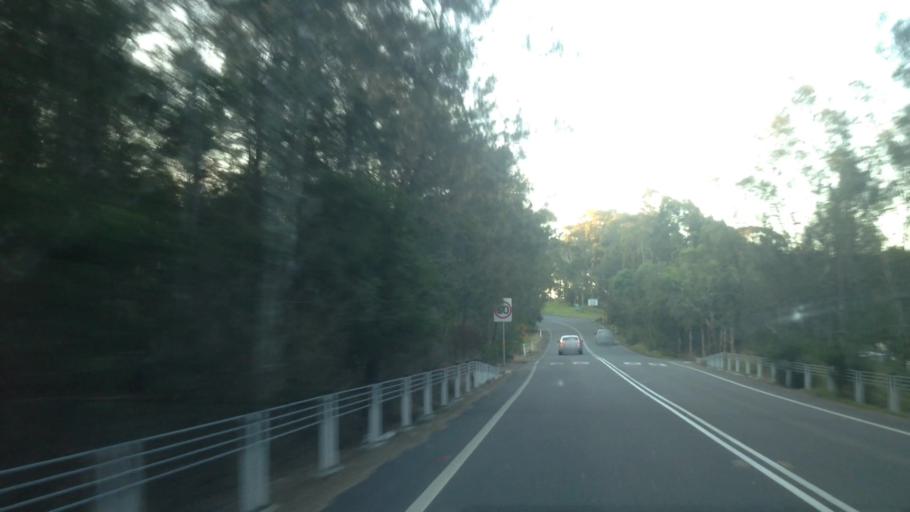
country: AU
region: New South Wales
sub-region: Wyong Shire
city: Kingfisher Shores
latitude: -33.1543
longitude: 151.5256
